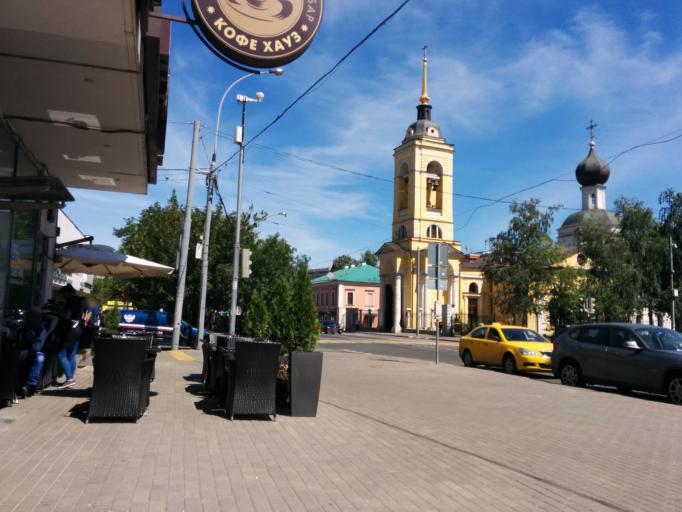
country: RU
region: Moscow
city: Zamoskvorech'ye
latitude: 55.7347
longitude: 37.6192
